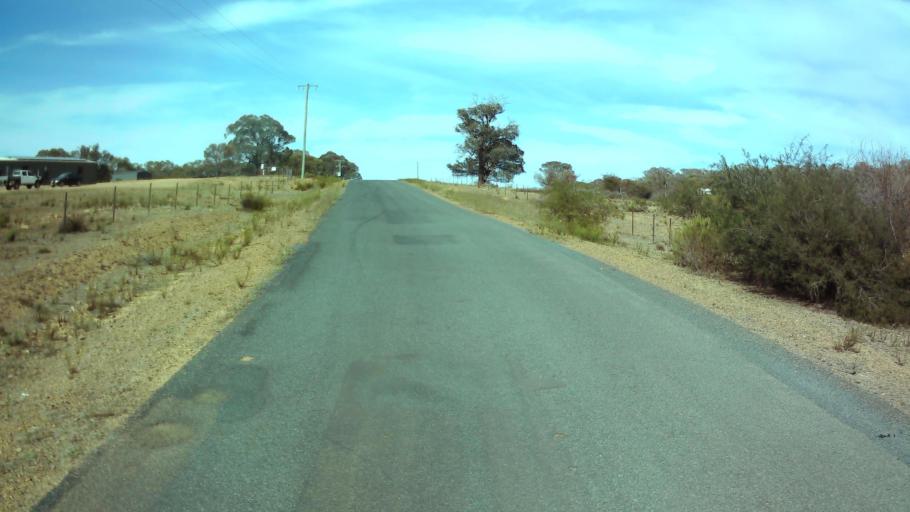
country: AU
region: New South Wales
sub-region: Weddin
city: Grenfell
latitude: -33.8778
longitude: 148.1996
